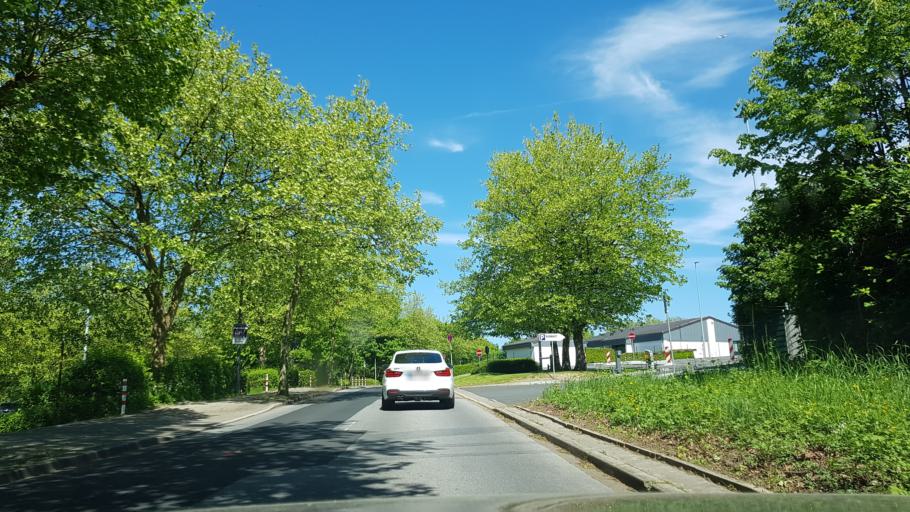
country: DE
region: North Rhine-Westphalia
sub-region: Regierungsbezirk Dusseldorf
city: Heiligenhaus
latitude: 51.3228
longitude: 6.9523
